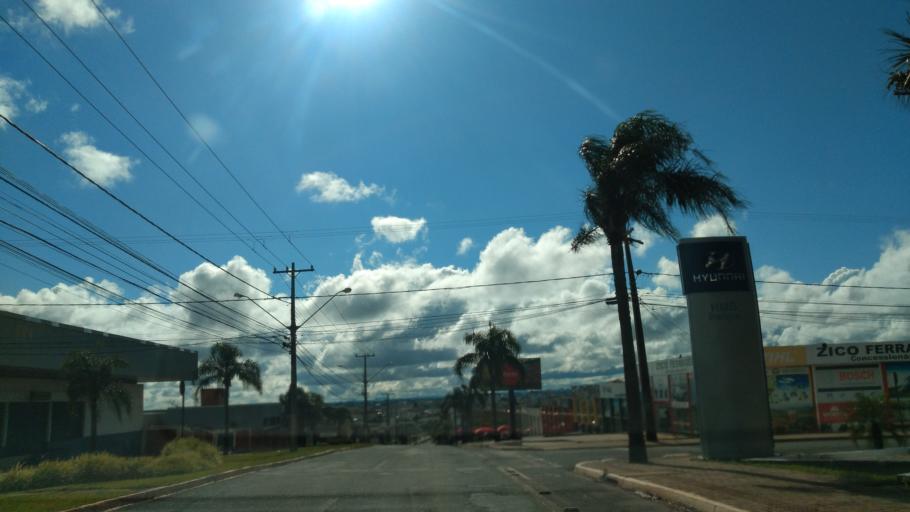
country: BR
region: Parana
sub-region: Guarapuava
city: Guarapuava
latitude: -25.3816
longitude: -51.4691
